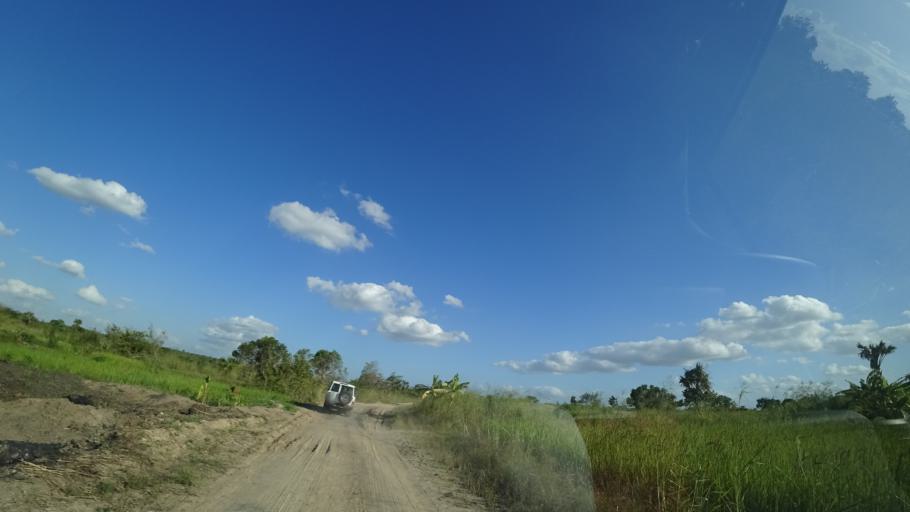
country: MZ
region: Sofala
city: Dondo
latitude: -19.3843
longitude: 34.5927
